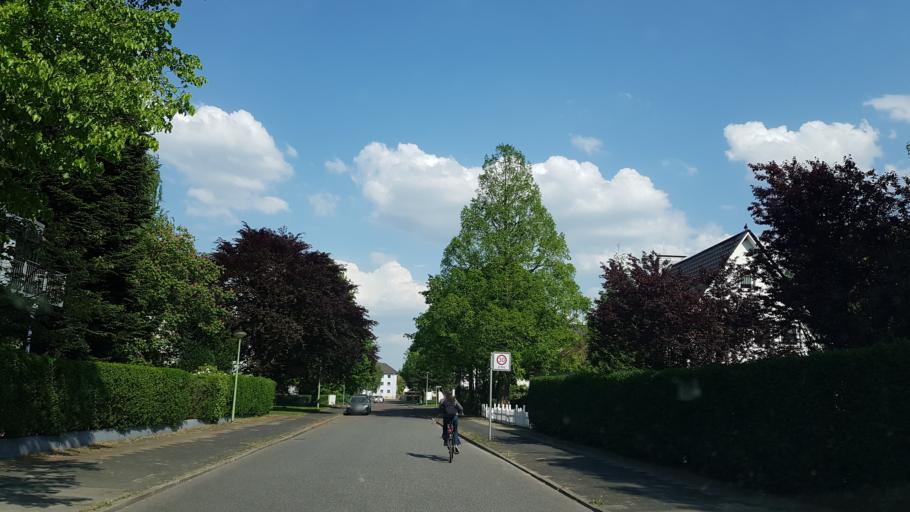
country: DE
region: Lower Saxony
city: Langen
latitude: 53.5779
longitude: 8.5920
